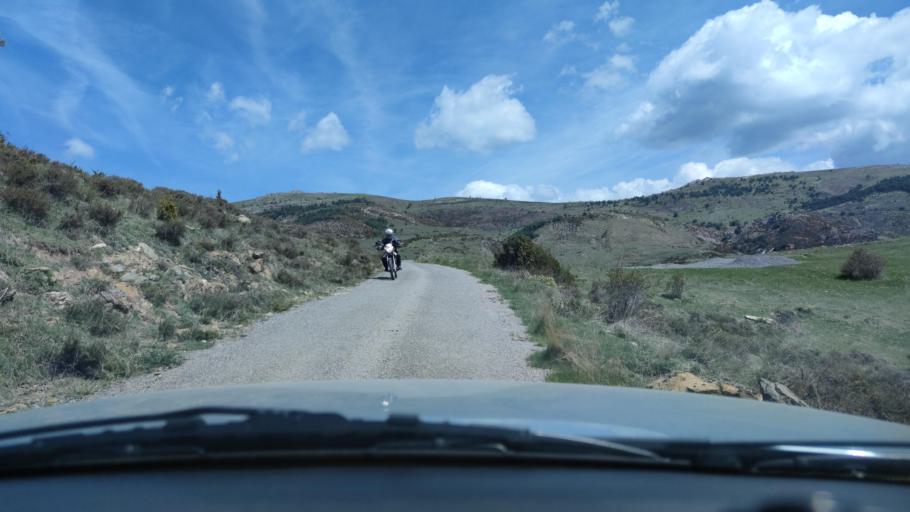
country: ES
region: Catalonia
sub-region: Provincia de Lleida
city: Sort
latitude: 42.3029
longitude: 1.1742
